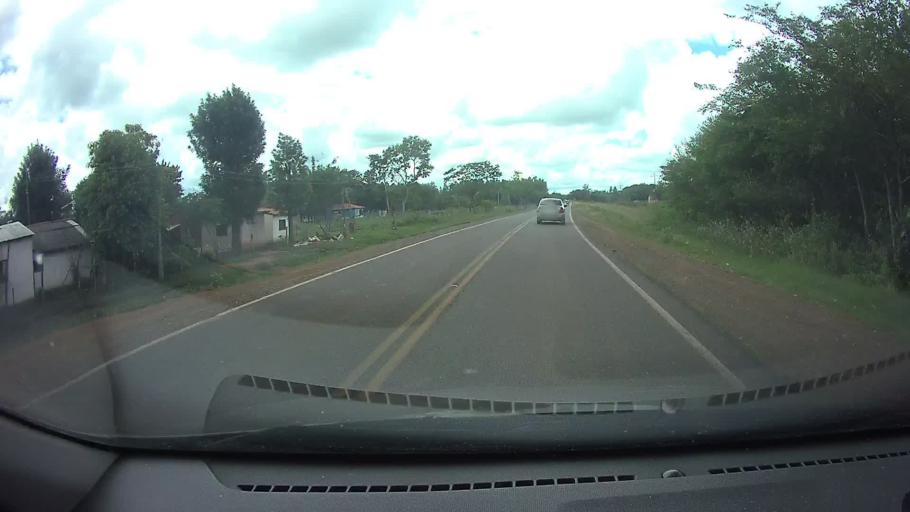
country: PY
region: Paraguari
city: Ybycui
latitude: -25.8980
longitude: -56.9690
